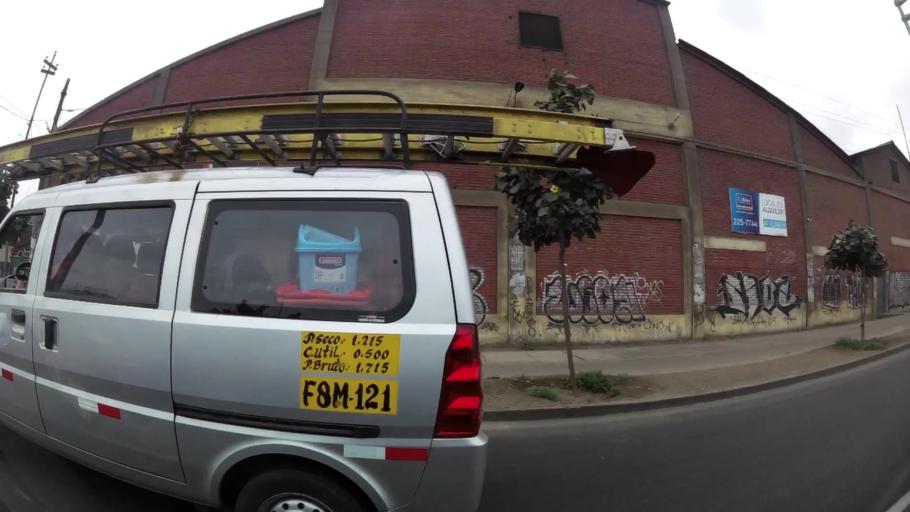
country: PE
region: Lima
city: Lima
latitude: -12.0448
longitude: -77.0586
